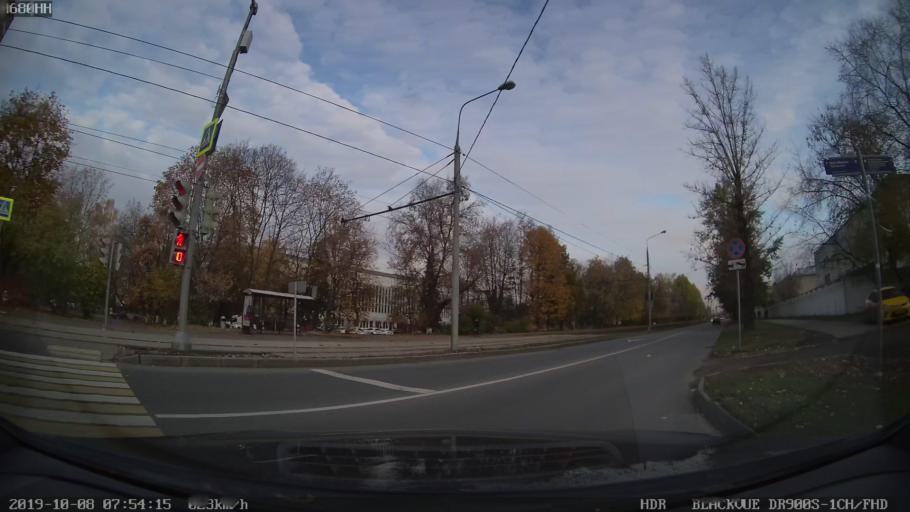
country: RU
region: Moscow
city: Shchukino
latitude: 55.7895
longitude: 37.4546
